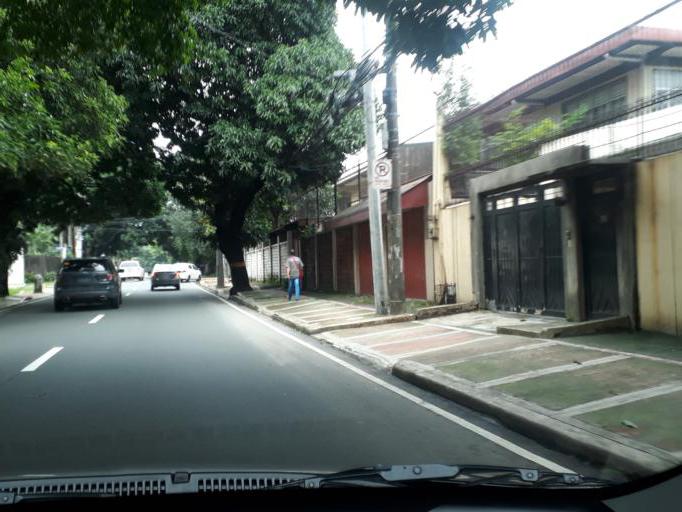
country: PH
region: Metro Manila
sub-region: San Juan
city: San Juan
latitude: 14.6189
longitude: 121.0316
